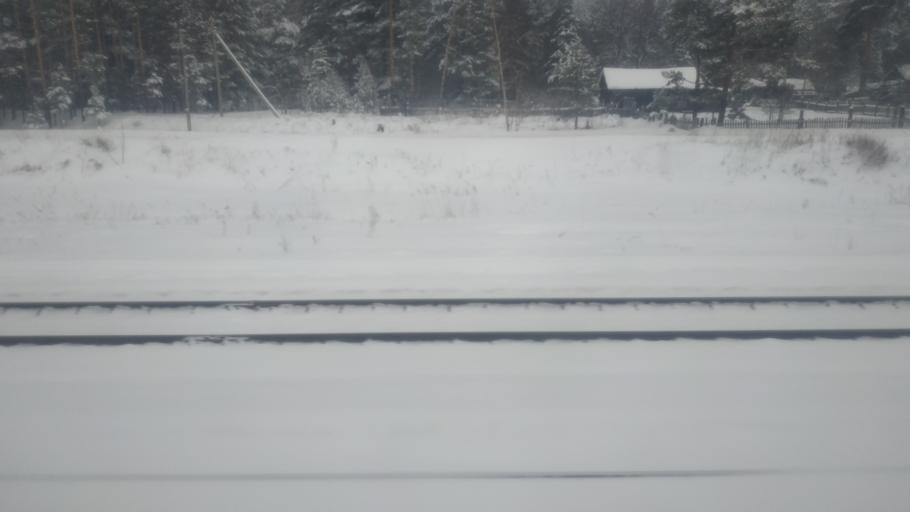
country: RU
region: Udmurtiya
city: Kama
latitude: 56.2947
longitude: 54.1156
